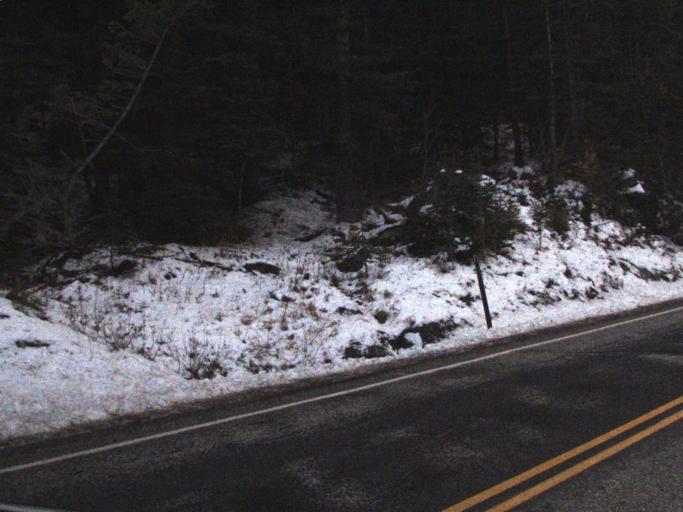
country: US
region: Washington
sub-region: Ferry County
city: Republic
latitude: 48.6046
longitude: -118.4668
